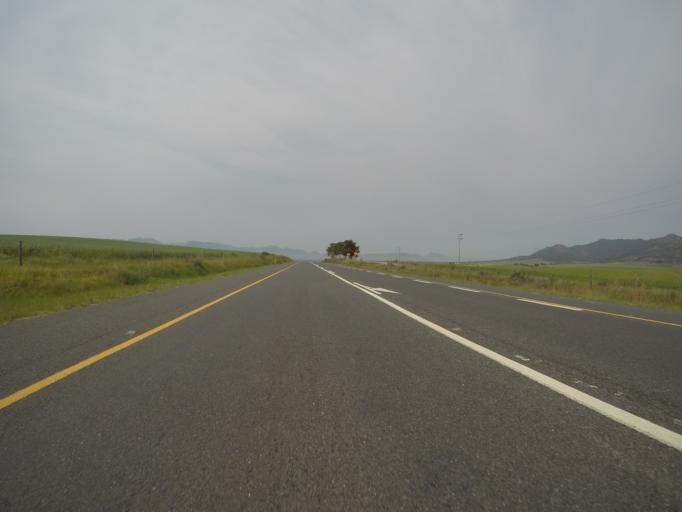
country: ZA
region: Western Cape
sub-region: West Coast District Municipality
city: Malmesbury
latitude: -33.5343
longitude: 18.8535
